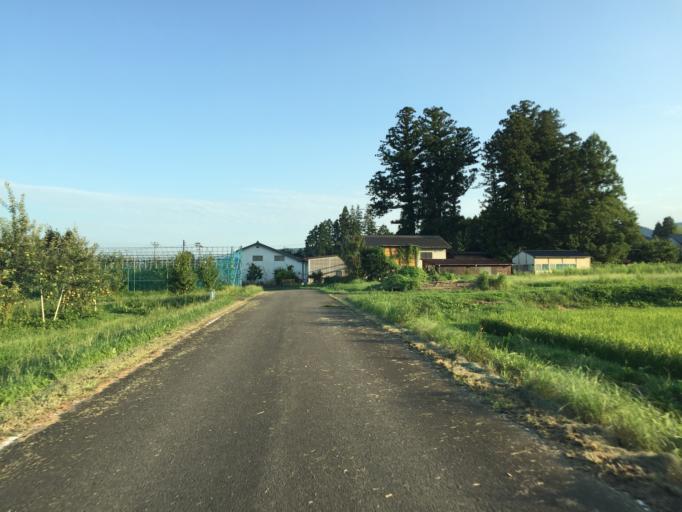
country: JP
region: Fukushima
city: Fukushima-shi
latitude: 37.7276
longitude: 140.3774
